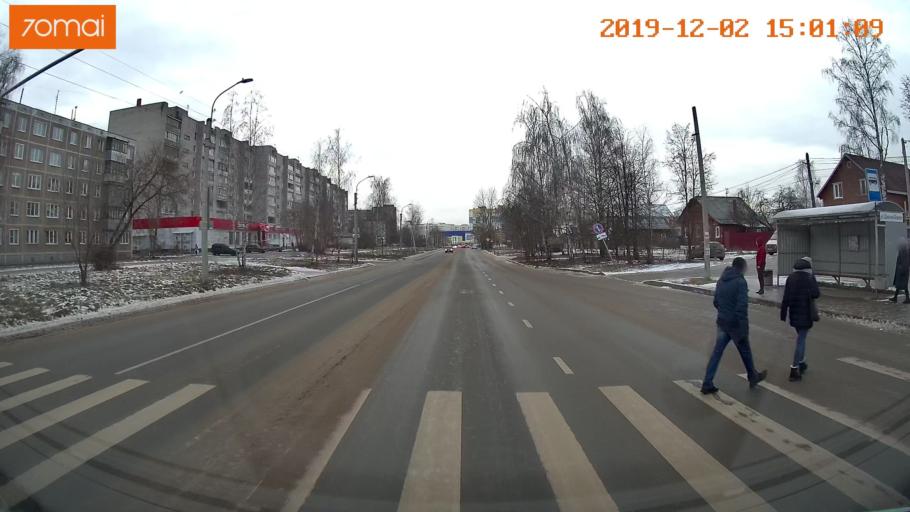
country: RU
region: Ivanovo
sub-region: Gorod Ivanovo
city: Ivanovo
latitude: 56.9734
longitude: 41.0004
